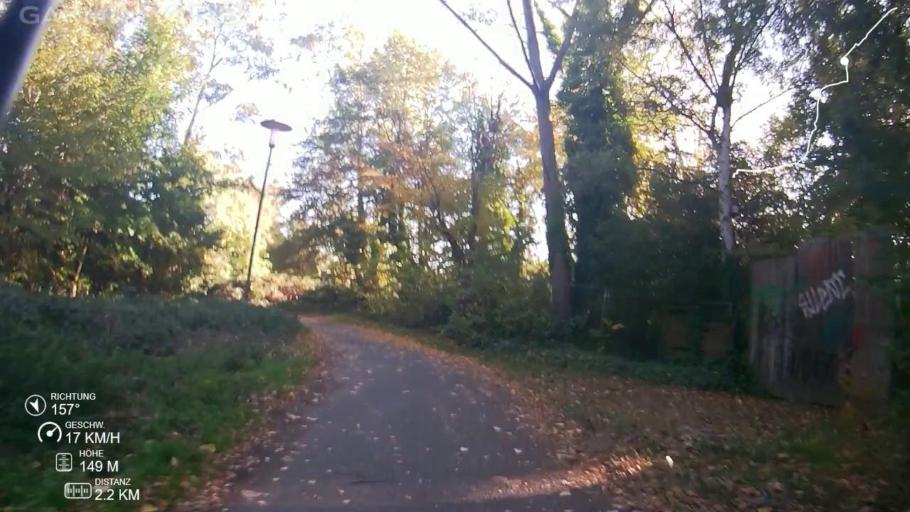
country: DE
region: Hesse
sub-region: Regierungsbezirk Darmstadt
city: Darmstadt
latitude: 49.9024
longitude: 8.6726
